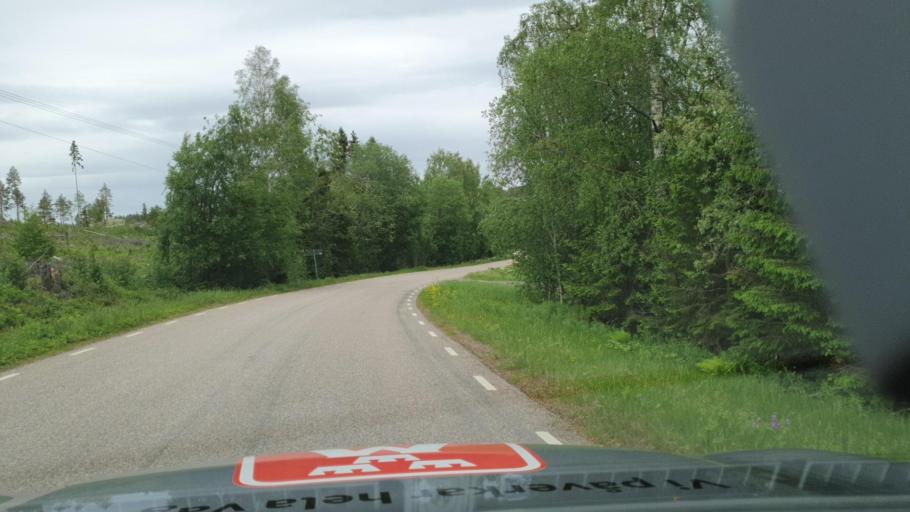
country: SE
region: Vaesternorrland
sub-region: Kramfors Kommun
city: Nordingra
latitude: 62.8787
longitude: 18.4227
